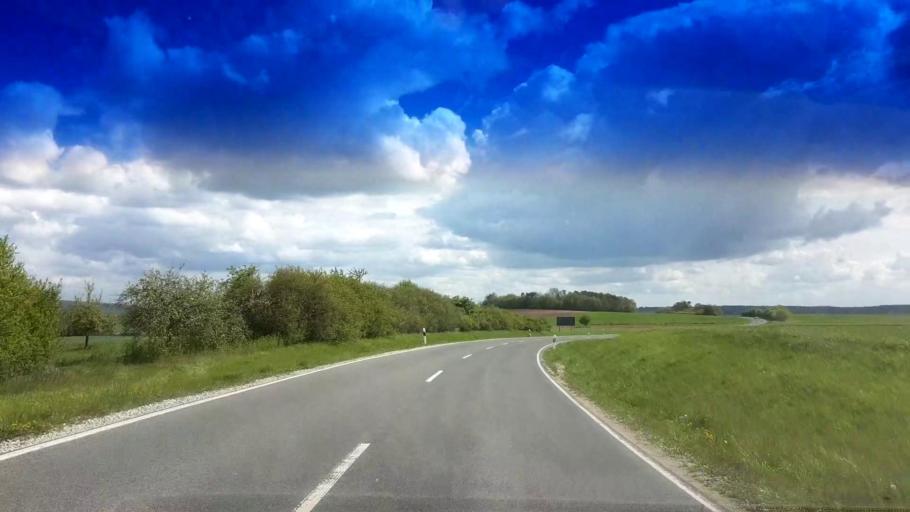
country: DE
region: Bavaria
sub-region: Upper Franconia
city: Stegaurach
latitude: 49.8407
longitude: 10.8381
